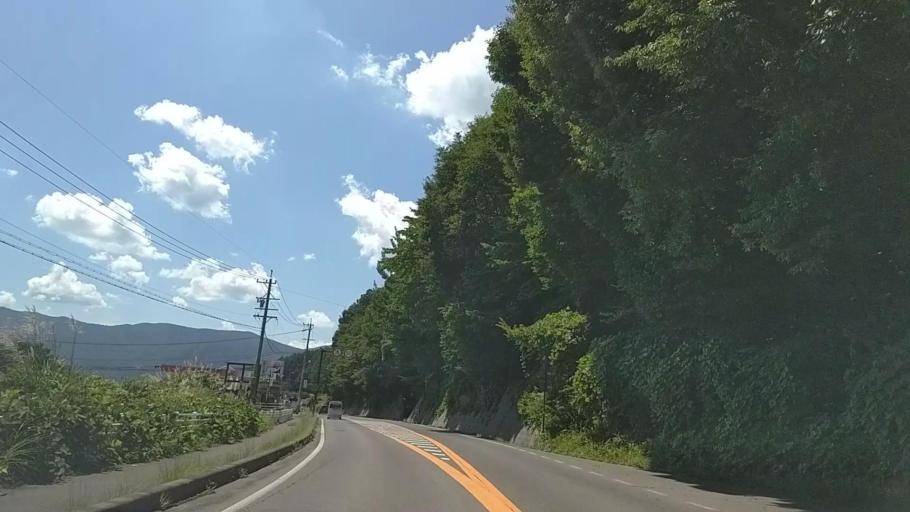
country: JP
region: Nagano
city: Chino
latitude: 36.0135
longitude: 138.1851
